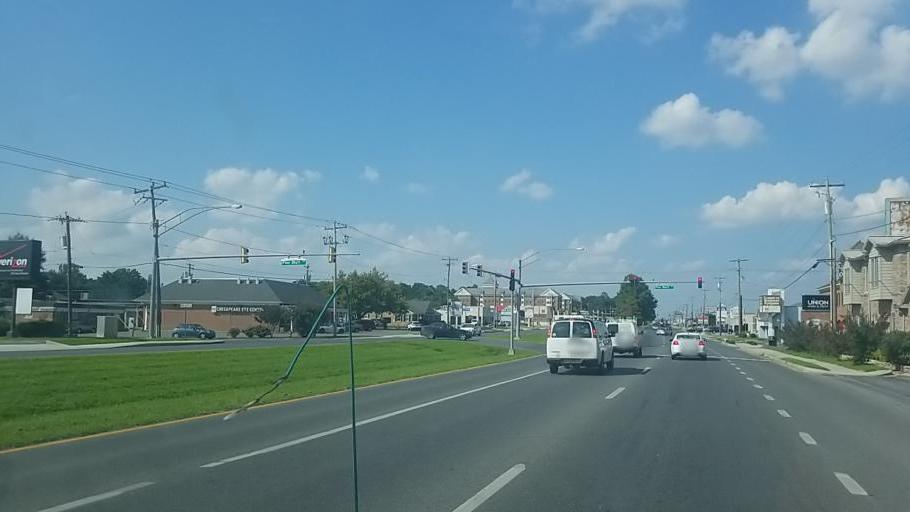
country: US
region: Maryland
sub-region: Wicomico County
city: Fruitland
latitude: 38.3383
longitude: -75.6068
